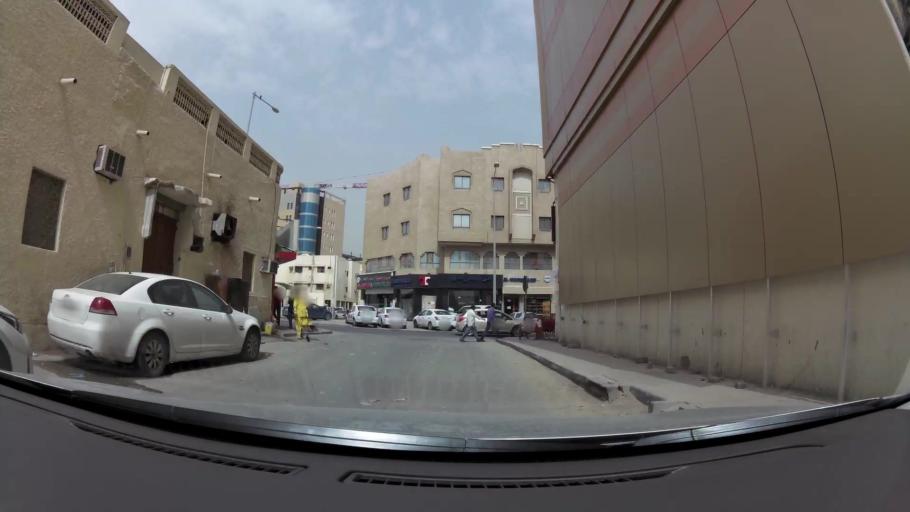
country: QA
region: Baladiyat ad Dawhah
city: Doha
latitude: 25.2705
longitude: 51.5435
